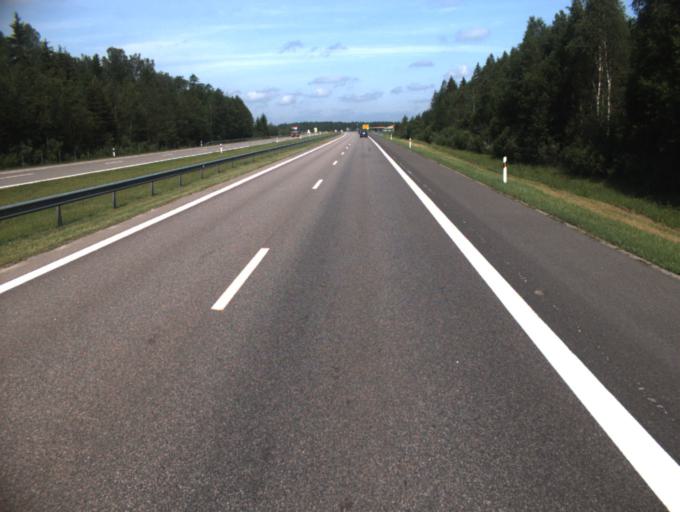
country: LT
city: Rietavas
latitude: 55.6820
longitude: 21.7021
